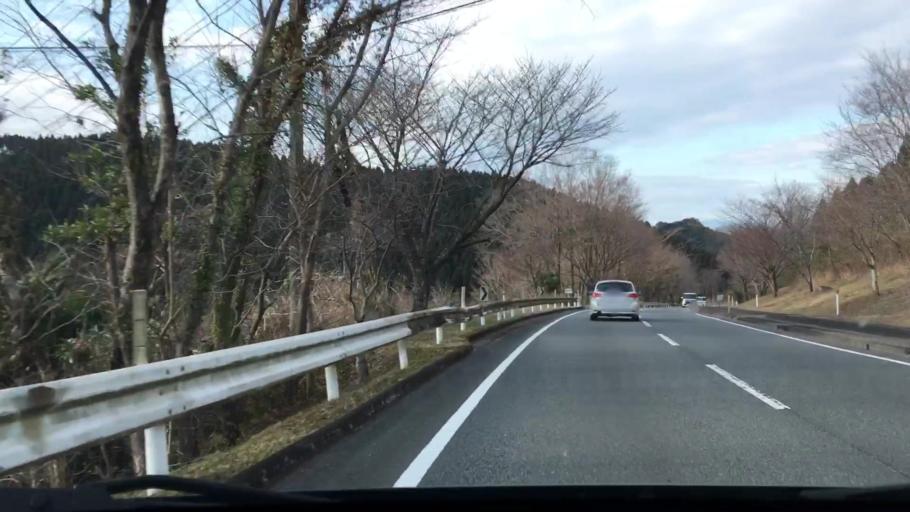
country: JP
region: Miyazaki
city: Miyazaki-shi
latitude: 31.8021
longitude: 131.3019
